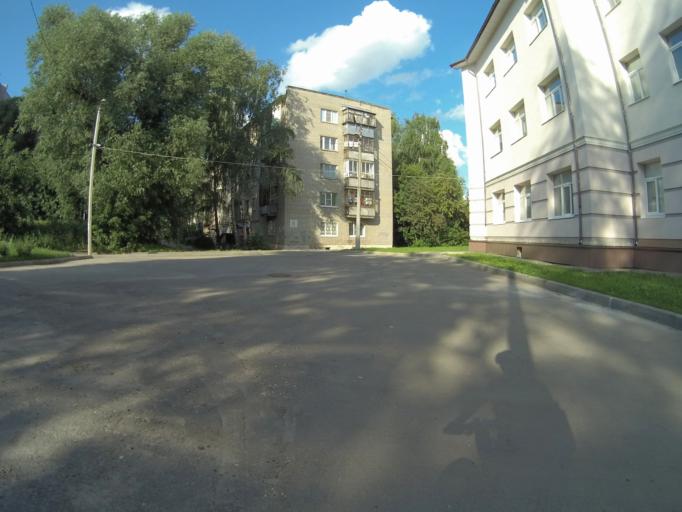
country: RU
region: Vladimir
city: Vladimir
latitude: 56.1420
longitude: 40.3833
